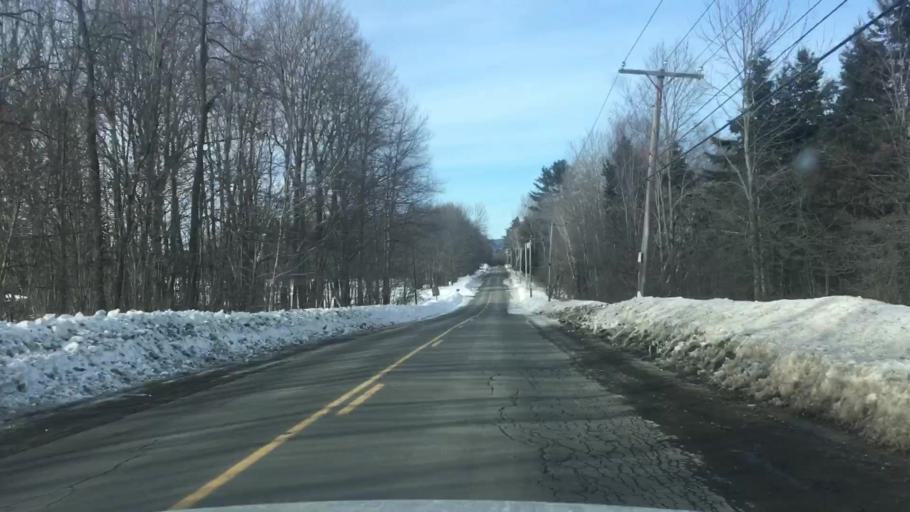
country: US
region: Maine
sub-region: Penobscot County
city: Charleston
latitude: 45.0319
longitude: -69.0316
